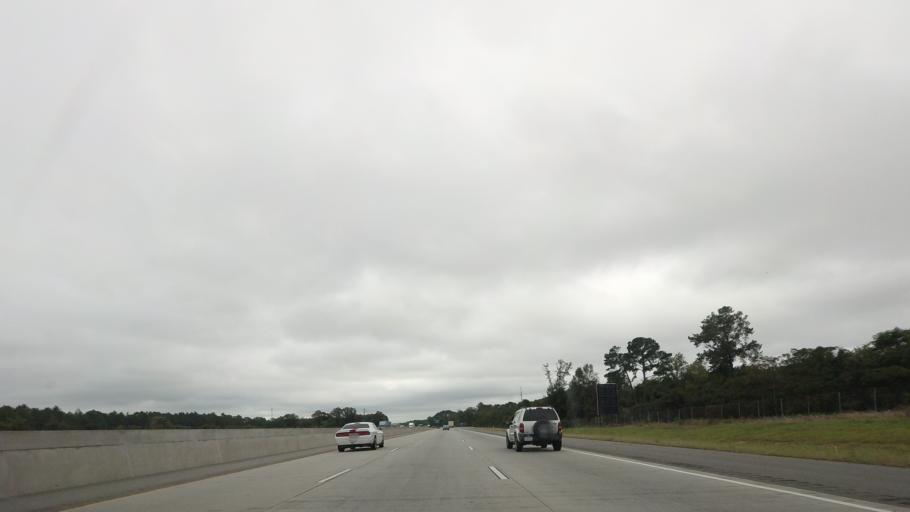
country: US
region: Georgia
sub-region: Tift County
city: Omega
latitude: 31.2919
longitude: -83.4770
